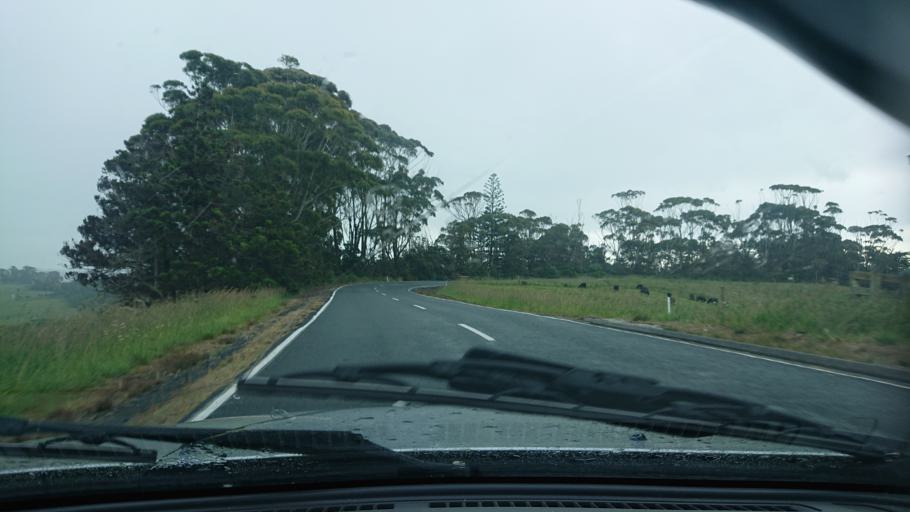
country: NZ
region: Auckland
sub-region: Auckland
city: Wellsford
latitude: -36.3308
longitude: 174.3874
